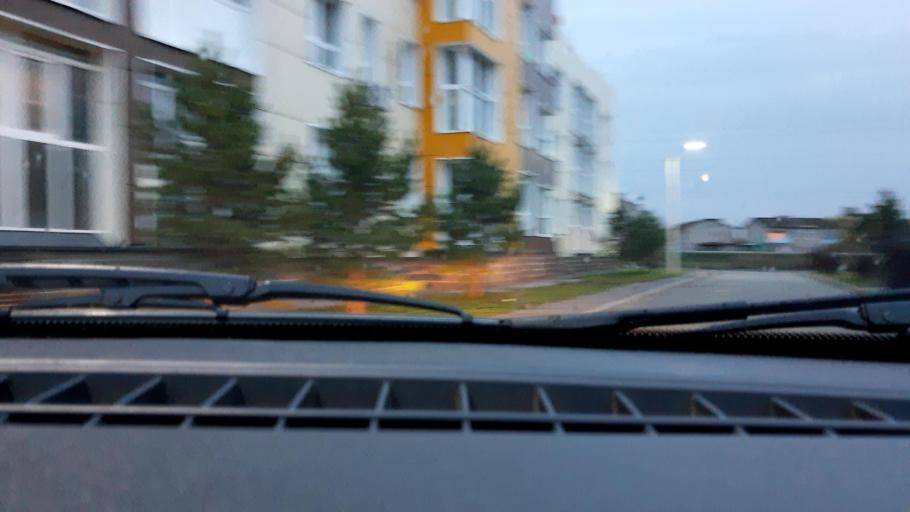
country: RU
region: Bashkortostan
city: Mikhaylovka
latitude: 54.7839
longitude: 55.8332
